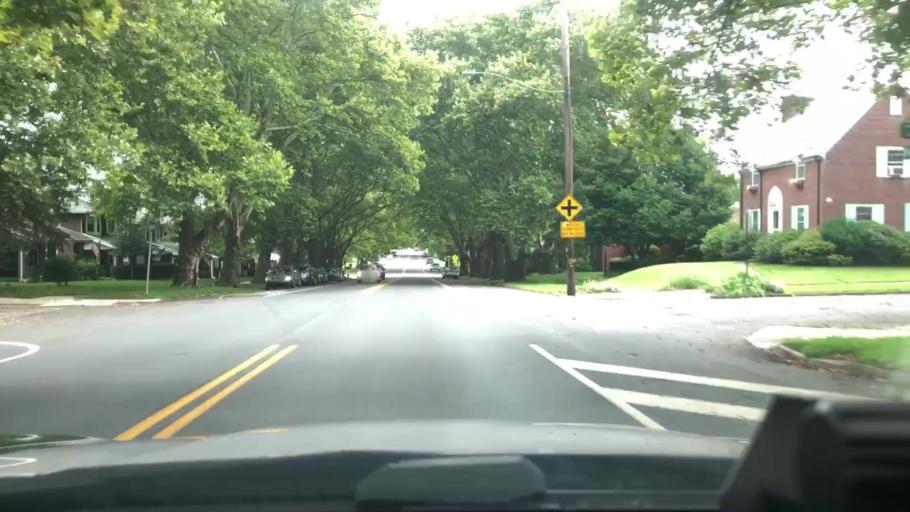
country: US
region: Pennsylvania
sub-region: Lehigh County
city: Fountain Hill
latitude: 40.6254
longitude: -75.4022
